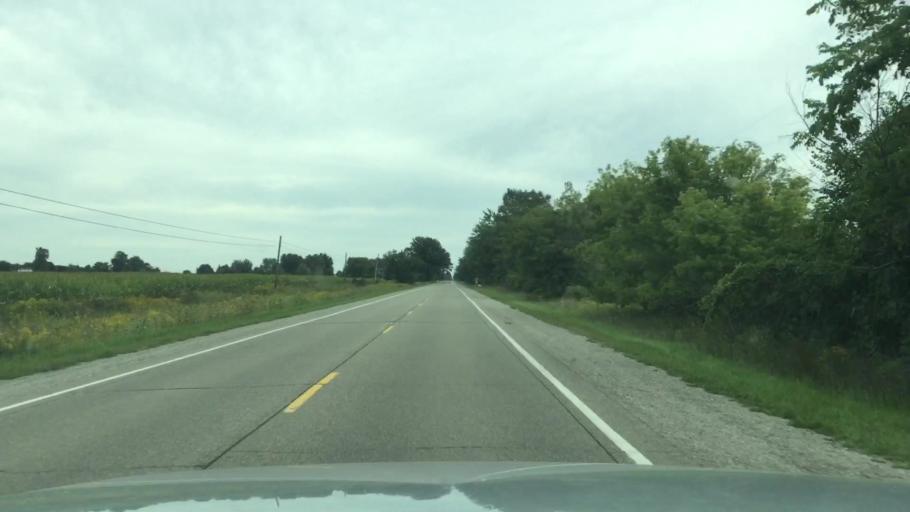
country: US
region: Michigan
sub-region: Genesee County
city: Swartz Creek
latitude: 42.9570
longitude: -83.8990
